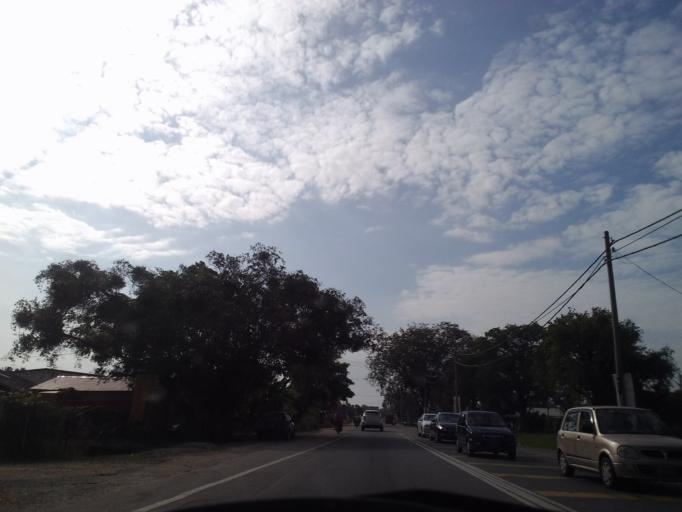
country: MY
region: Kedah
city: Alor Setar
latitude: 6.0413
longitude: 100.3758
